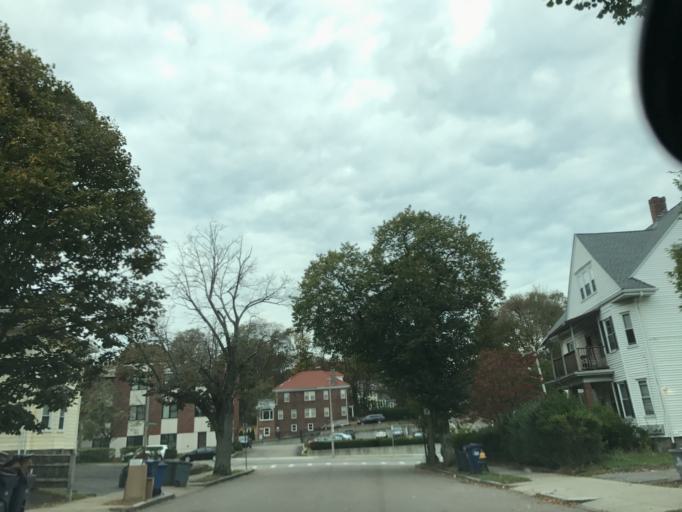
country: US
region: Massachusetts
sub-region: Norfolk County
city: Brookline
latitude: 42.3444
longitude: -71.1527
